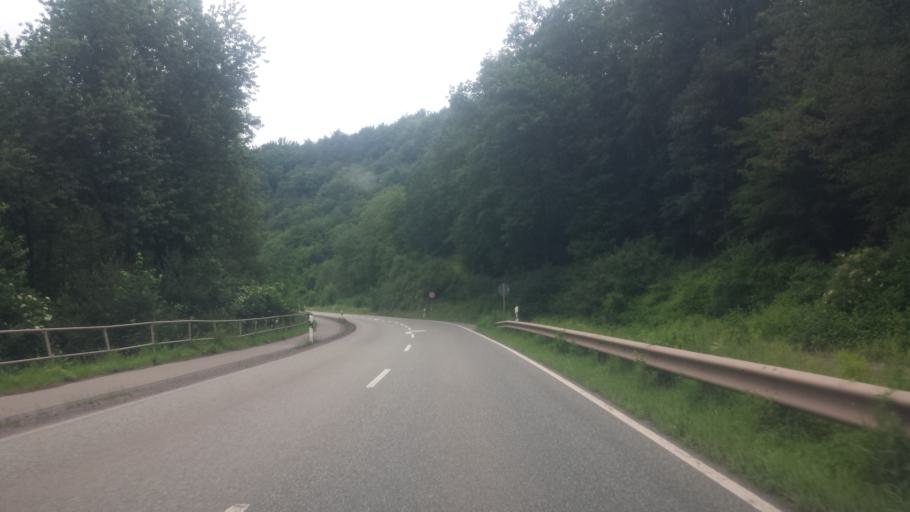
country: DE
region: Rheinland-Pfalz
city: Eschbach
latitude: 49.1605
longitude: 8.0062
